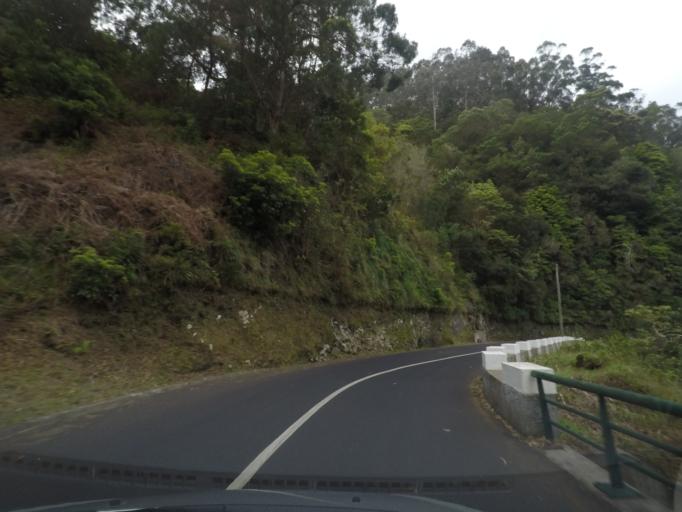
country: PT
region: Madeira
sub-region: Santa Cruz
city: Camacha
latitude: 32.7485
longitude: -16.8326
